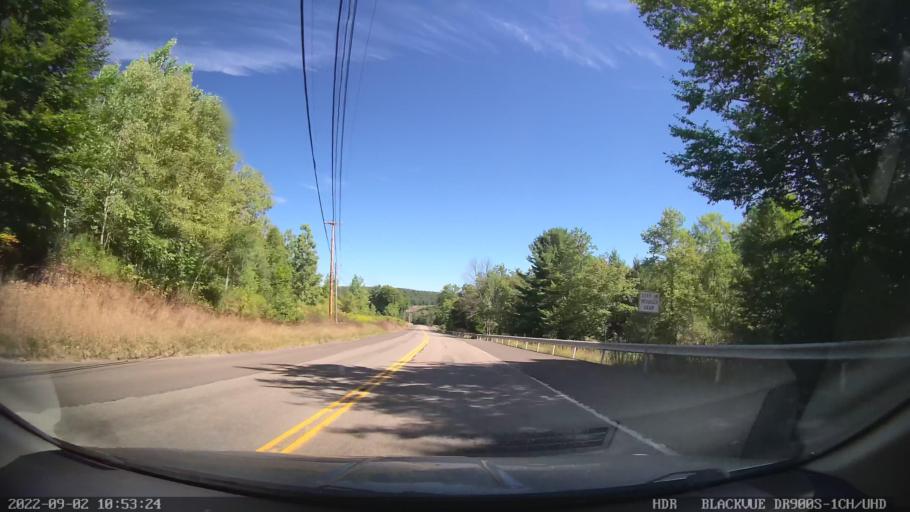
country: US
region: Pennsylvania
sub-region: Tioga County
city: Blossburg
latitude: 41.6454
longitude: -77.0975
